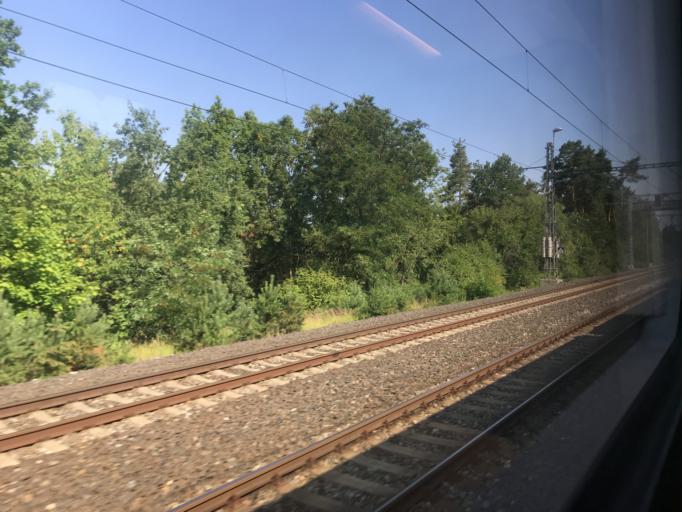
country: CZ
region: Central Bohemia
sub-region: Okres Praha-Vychod
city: Mnichovice
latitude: 49.8998
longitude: 14.7272
